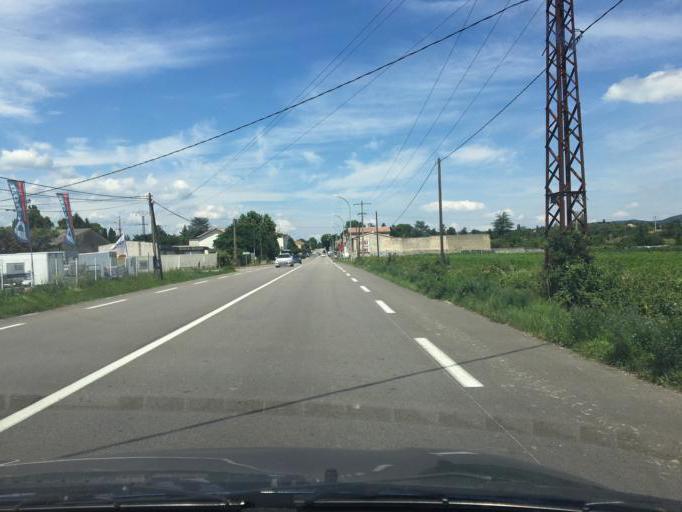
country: FR
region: Rhone-Alpes
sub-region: Departement de la Drome
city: Saulce-sur-Rhone
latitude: 44.6888
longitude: 4.7971
